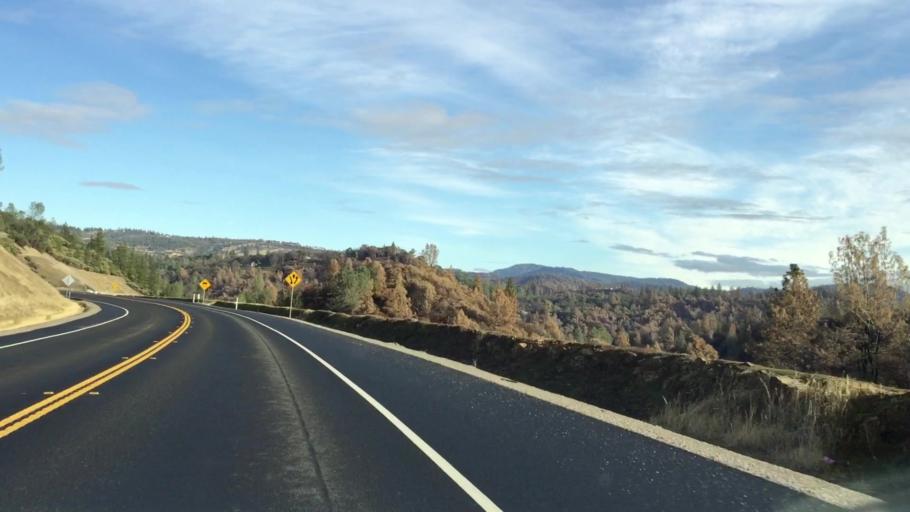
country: US
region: California
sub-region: Butte County
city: Paradise
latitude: 39.6582
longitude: -121.5361
